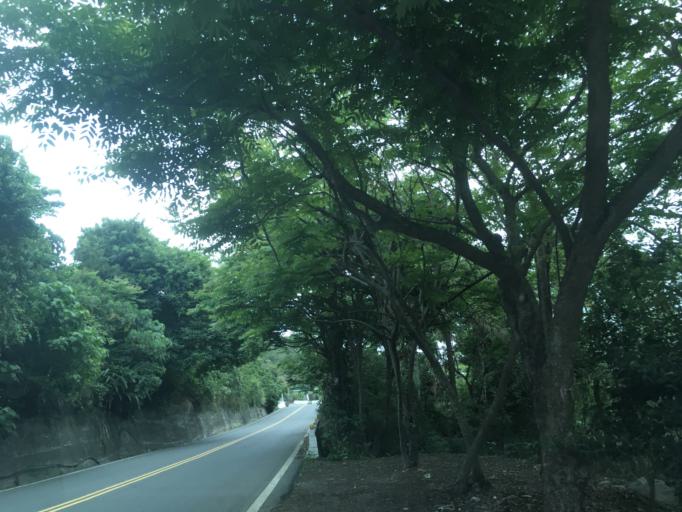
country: TW
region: Taiwan
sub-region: Taitung
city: Taitung
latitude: 22.8182
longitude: 121.1363
